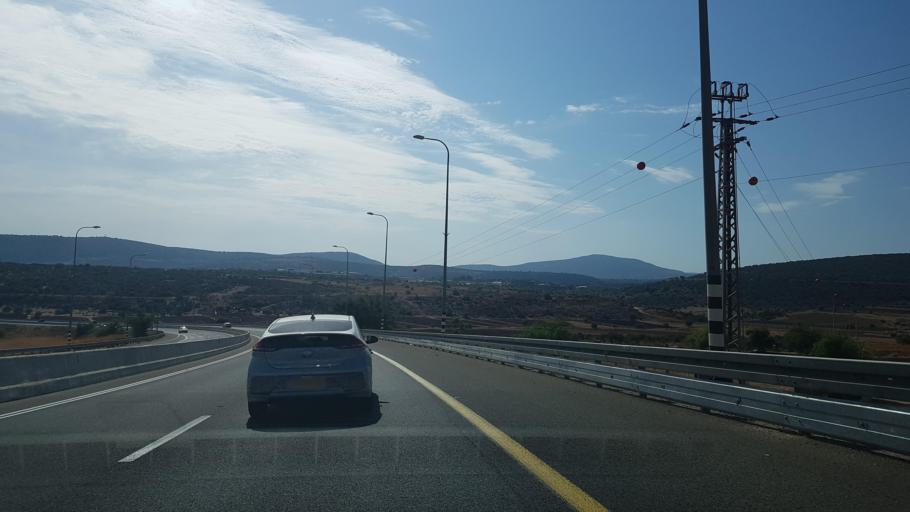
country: IL
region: Northern District
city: Maghar
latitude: 32.8853
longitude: 35.4739
